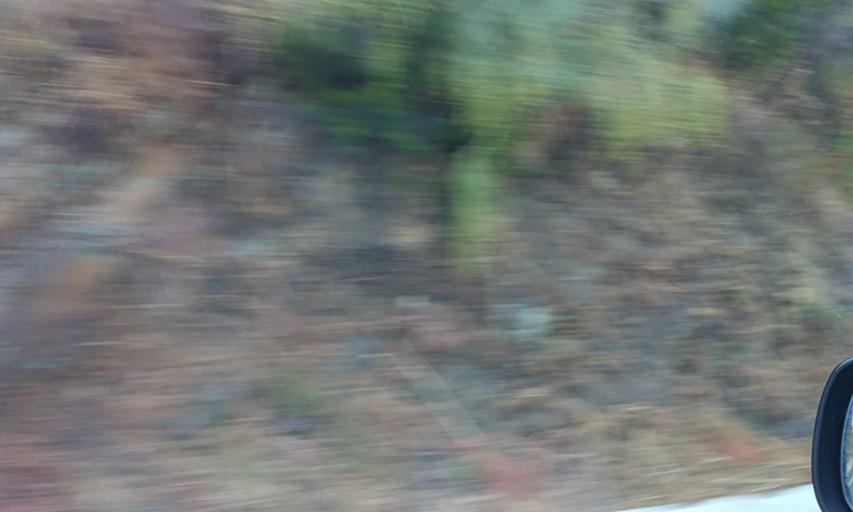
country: PT
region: Viseu
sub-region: Sao Joao da Pesqueira
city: Sao Joao da Pesqueira
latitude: 41.2158
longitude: -7.4301
